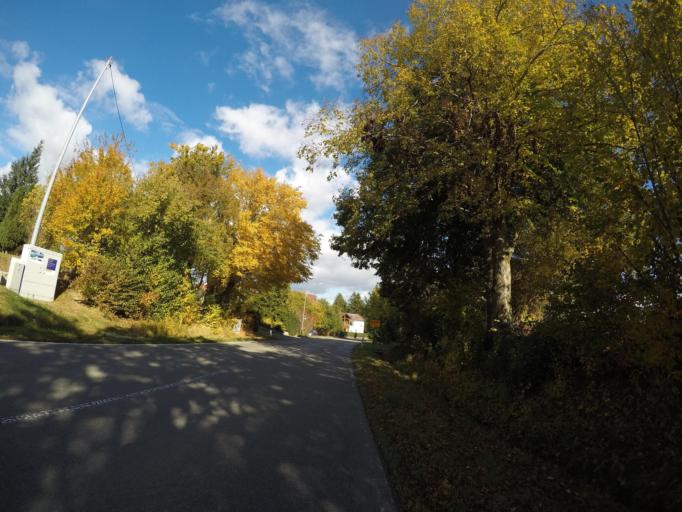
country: DE
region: Baden-Wuerttemberg
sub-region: Tuebingen Region
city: Grundsheim
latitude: 48.1661
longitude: 9.6823
